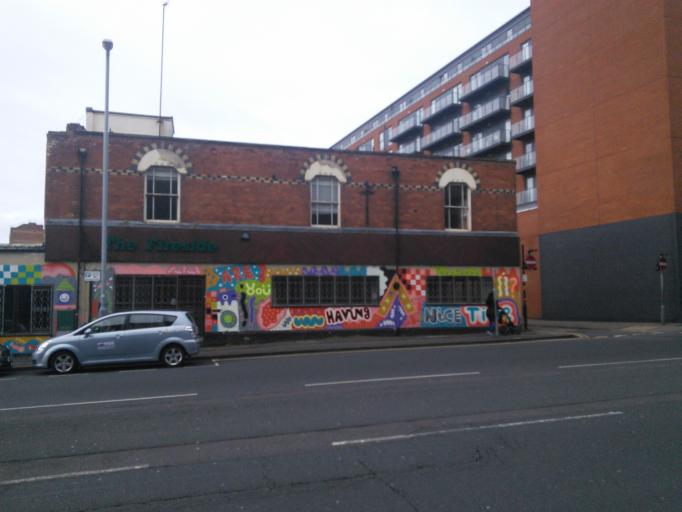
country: GB
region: England
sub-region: City and Borough of Birmingham
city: Birmingham
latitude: 52.4738
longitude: -1.8941
